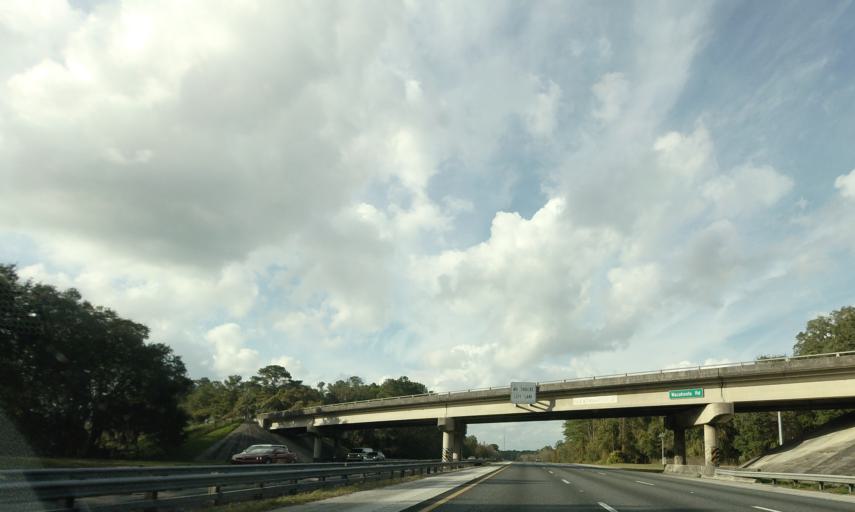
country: US
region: Florida
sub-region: Alachua County
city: Gainesville
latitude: 29.5216
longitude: -82.3097
